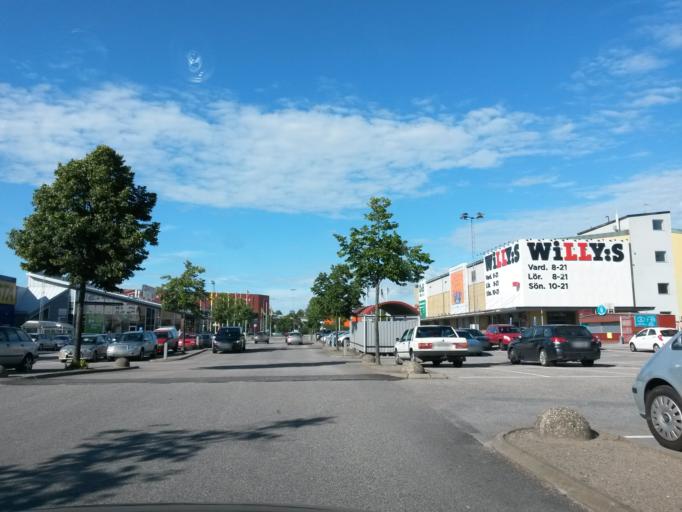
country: SE
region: Vaestra Goetaland
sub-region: Boras Kommun
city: Boras
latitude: 57.7314
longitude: 12.9328
